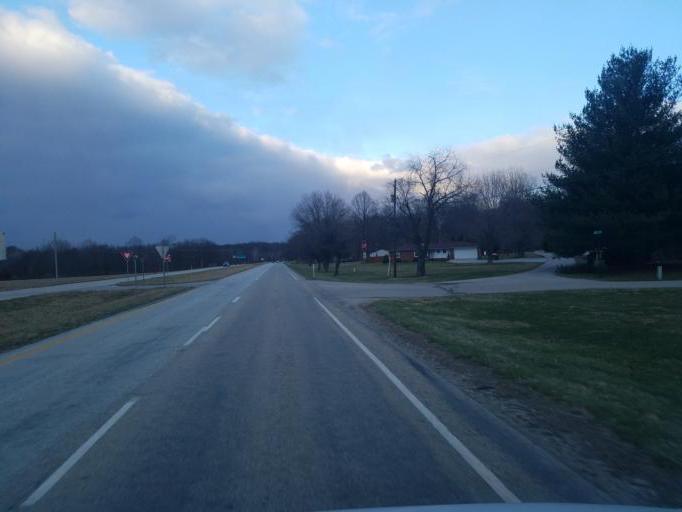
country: US
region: Indiana
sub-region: Henry County
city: Knightstown
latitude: 39.8011
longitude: -85.5072
